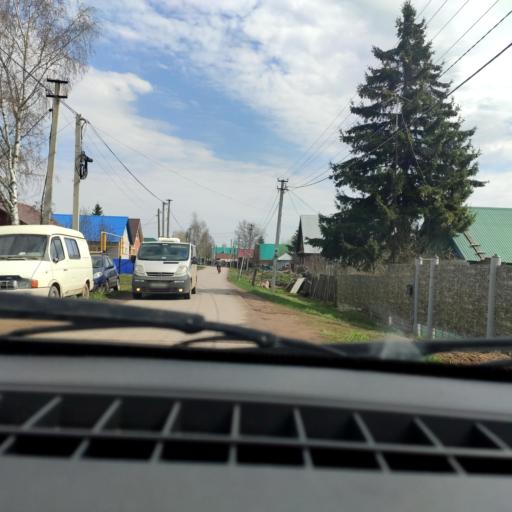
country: RU
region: Bashkortostan
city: Avdon
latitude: 54.6443
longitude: 55.7442
